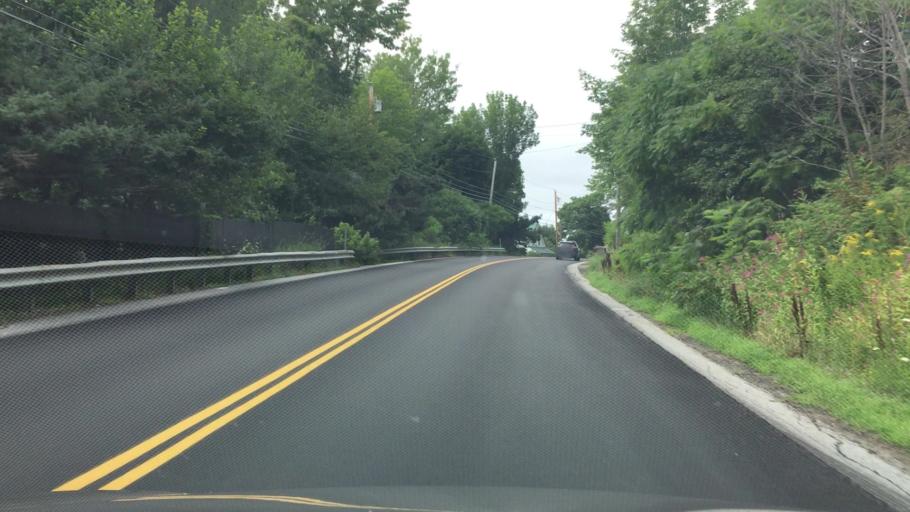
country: US
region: Maine
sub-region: Waldo County
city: Winterport
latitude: 44.6196
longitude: -68.8304
